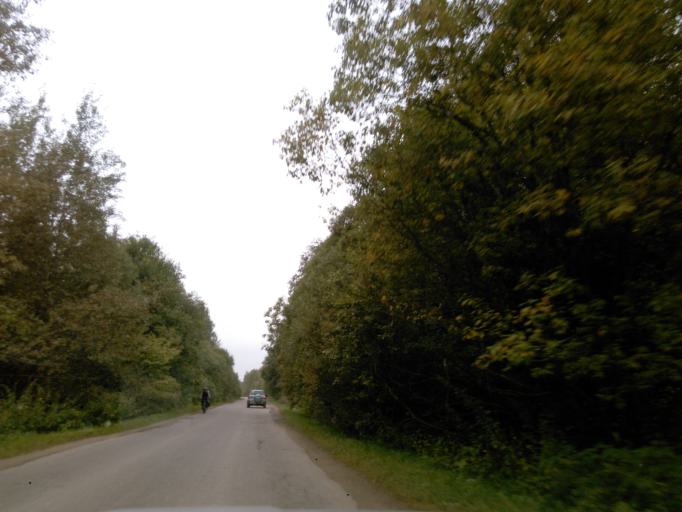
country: RU
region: Moskovskaya
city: Mendeleyevo
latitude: 56.1027
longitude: 37.2694
